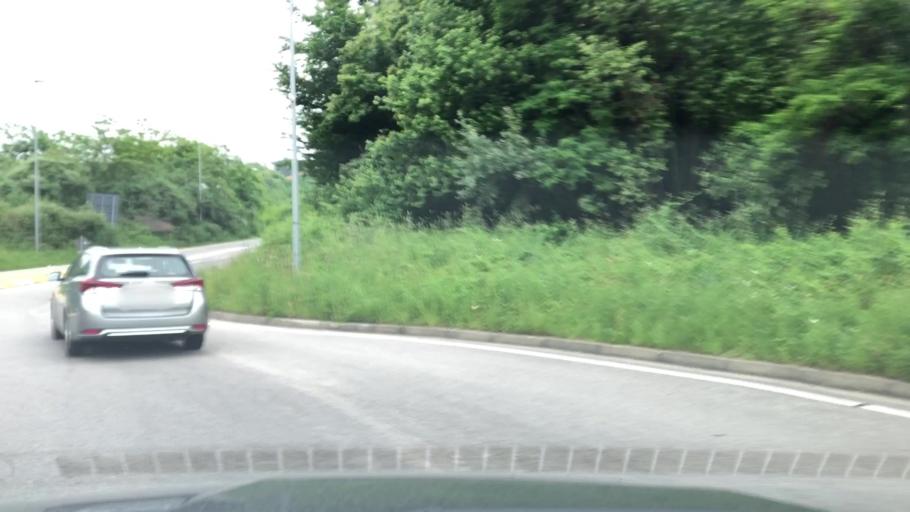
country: IT
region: Lombardy
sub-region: Provincia di Como
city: Casnate Con Bernate
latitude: 45.7674
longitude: 9.0750
